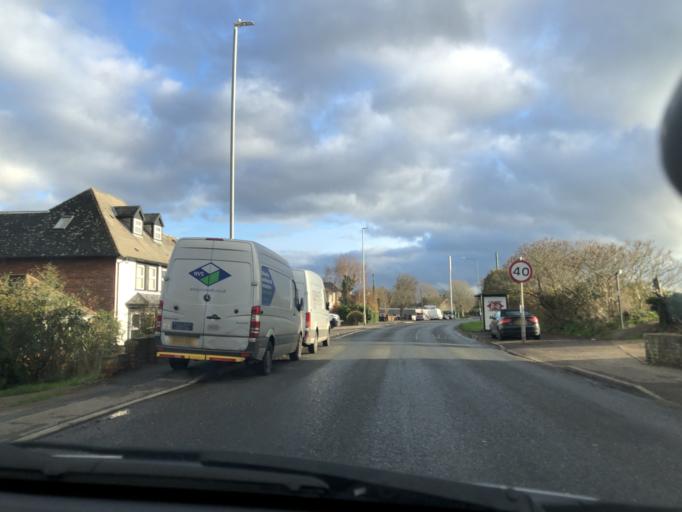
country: GB
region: England
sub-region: Kent
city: Dartford
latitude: 51.4311
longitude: 0.2194
